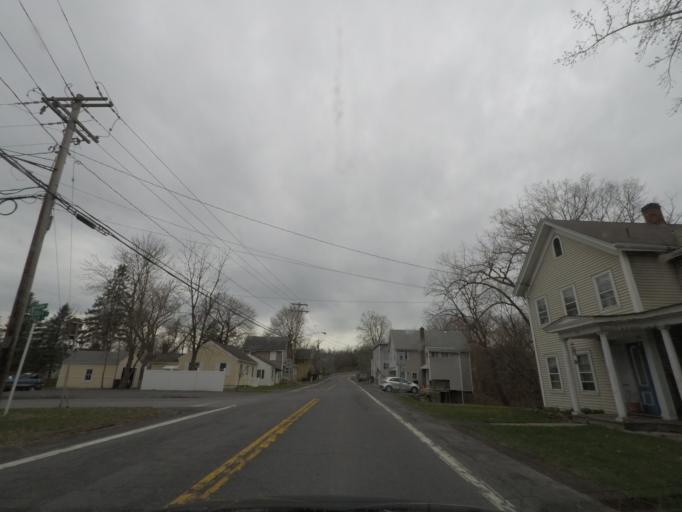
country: US
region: New York
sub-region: Albany County
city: Ravena
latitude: 42.5320
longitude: -73.8472
